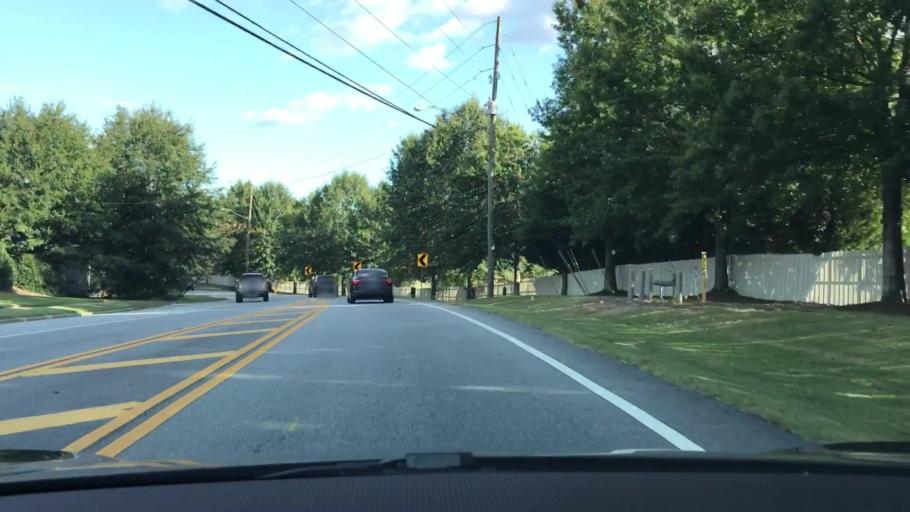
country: US
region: Georgia
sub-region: Gwinnett County
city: Dacula
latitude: 34.0414
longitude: -83.9197
